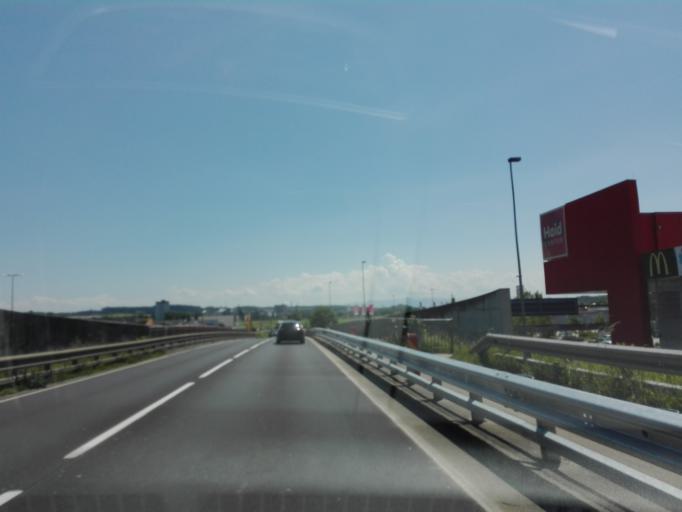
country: AT
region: Upper Austria
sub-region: Politischer Bezirk Linz-Land
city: Traun
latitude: 48.1967
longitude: 14.2489
